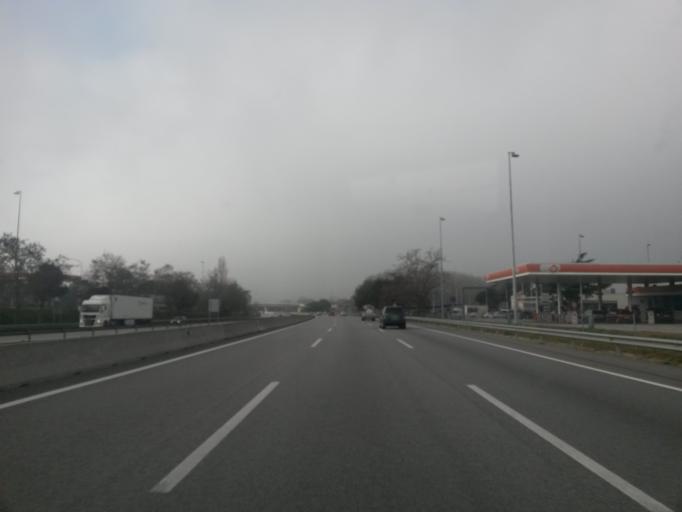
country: ES
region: Catalonia
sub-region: Provincia de Barcelona
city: Llinars del Valles
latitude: 41.6478
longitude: 2.4265
